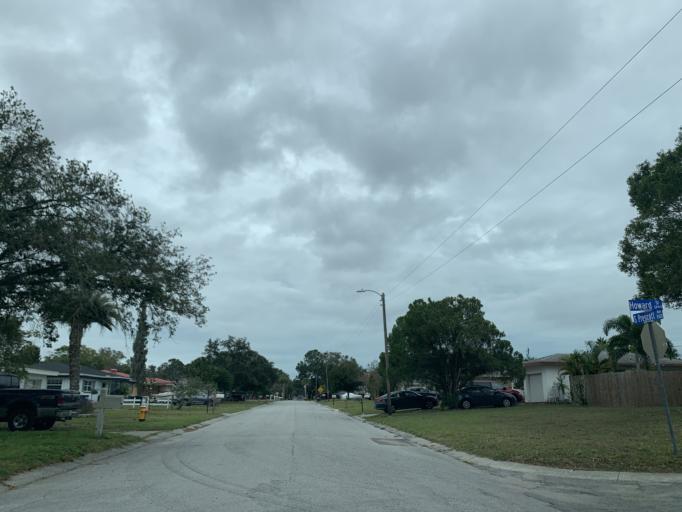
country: US
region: Florida
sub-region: Pinellas County
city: Belleair
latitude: 27.9408
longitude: -82.7843
